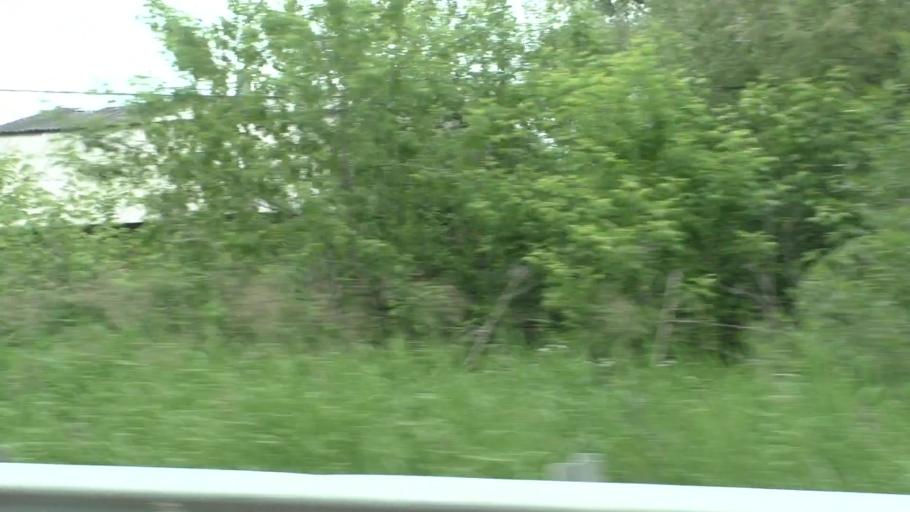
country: RU
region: Moskovskaya
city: Yegor'yevsk
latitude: 55.4005
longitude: 39.0063
